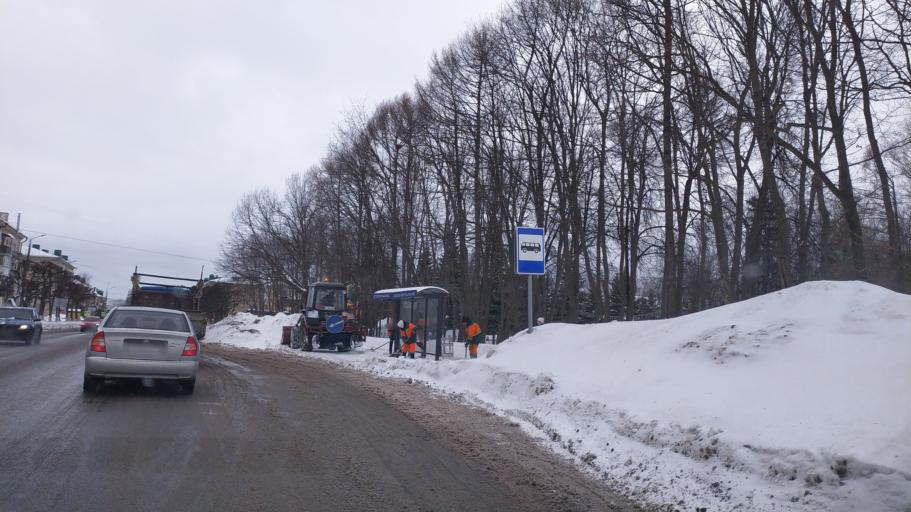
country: RU
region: Chuvashia
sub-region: Cheboksarskiy Rayon
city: Cheboksary
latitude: 56.1178
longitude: 47.2618
